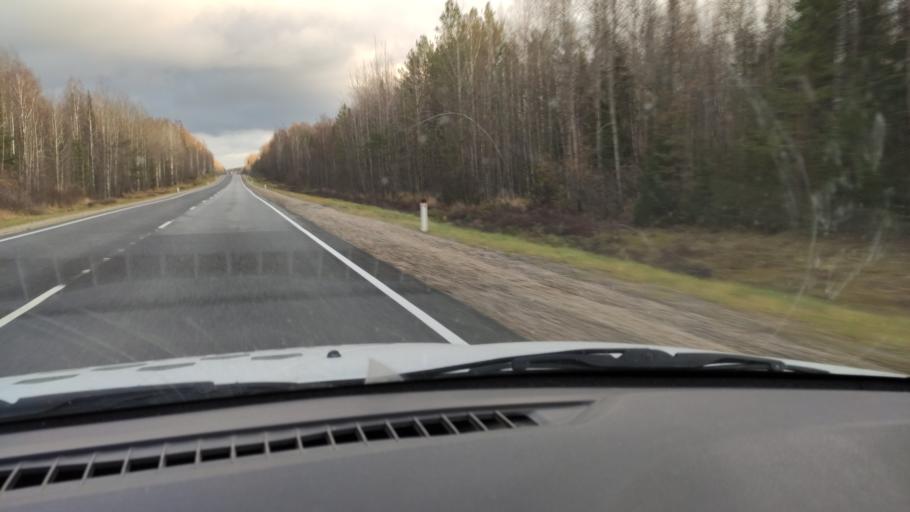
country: RU
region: Kirov
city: Chernaya Kholunitsa
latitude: 58.7895
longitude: 51.8912
